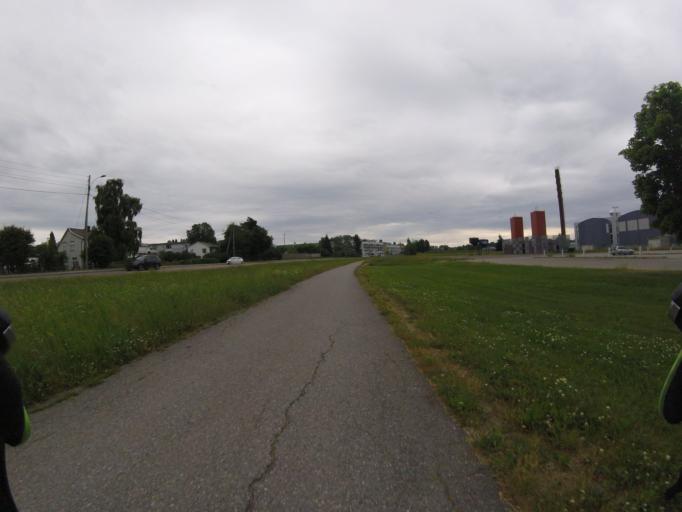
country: NO
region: Akershus
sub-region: Skedsmo
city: Lillestrom
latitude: 59.9720
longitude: 11.0447
